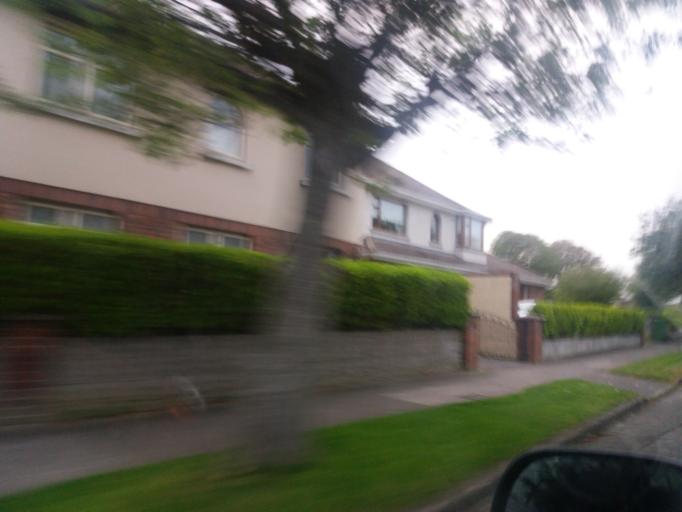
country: IE
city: Bayside
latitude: 53.3837
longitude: -6.1509
